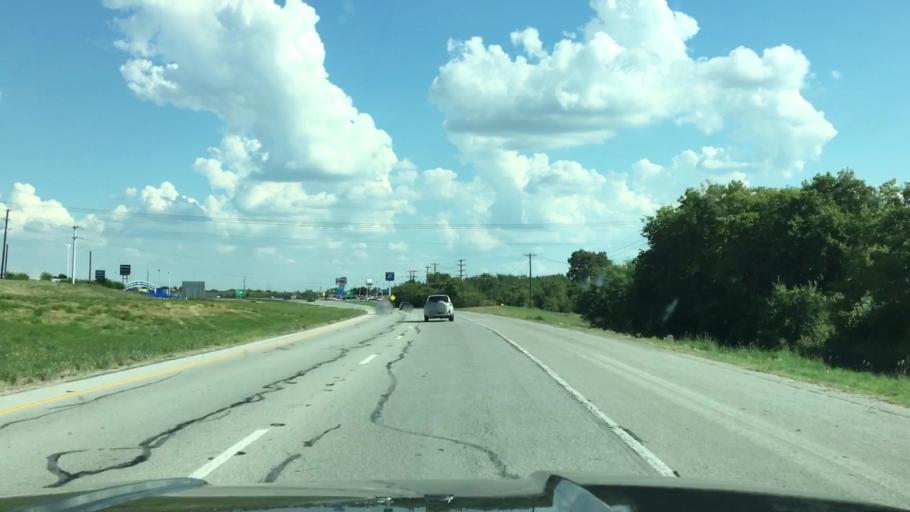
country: US
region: Texas
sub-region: Wise County
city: Decatur
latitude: 33.2189
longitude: -97.5885
